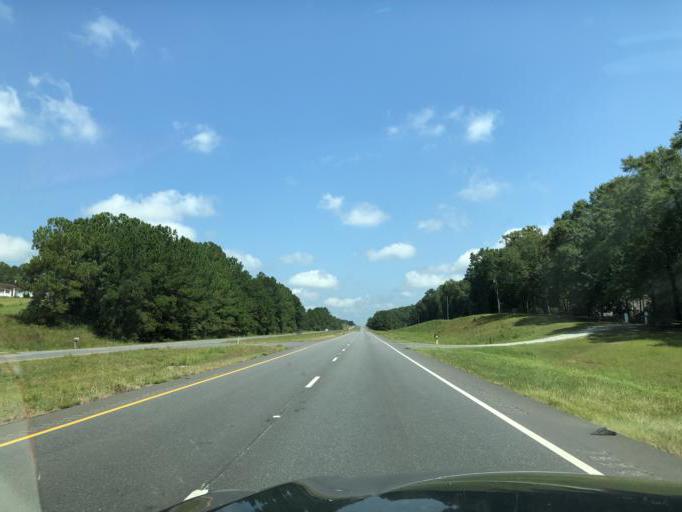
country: US
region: Alabama
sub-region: Henry County
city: Headland
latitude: 31.4652
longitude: -85.3060
